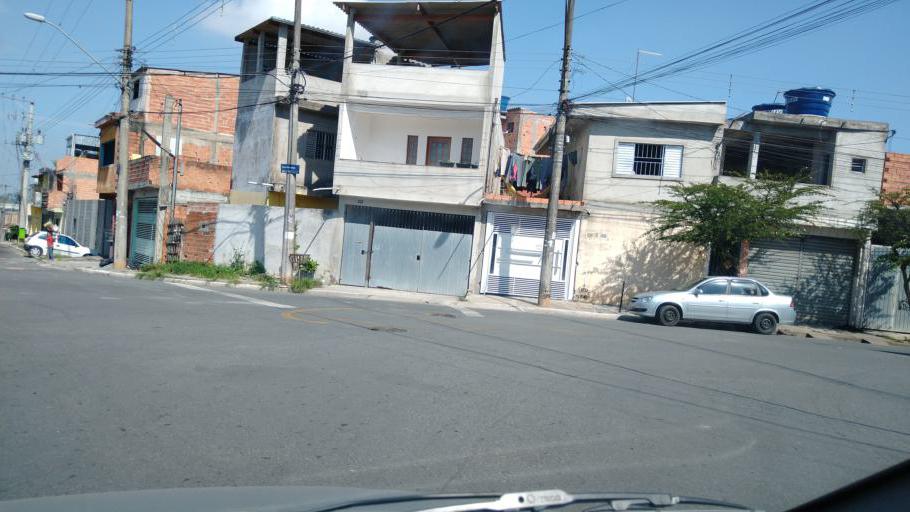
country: BR
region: Sao Paulo
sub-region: Aruja
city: Aruja
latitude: -23.4091
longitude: -46.3937
